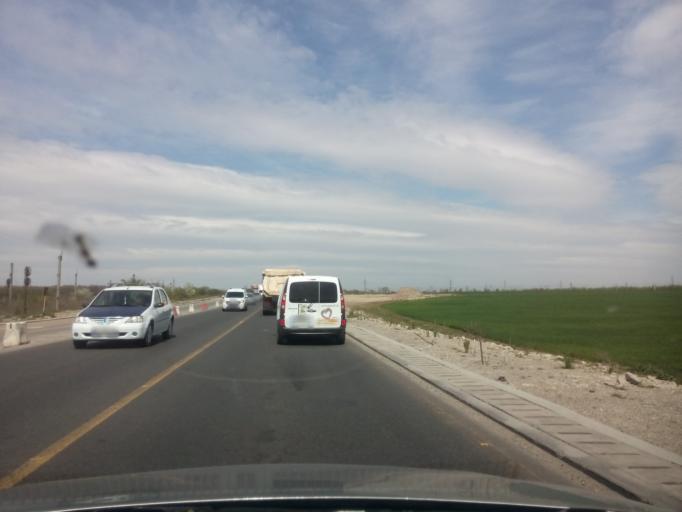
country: RO
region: Ilfov
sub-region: Comuna Pantelimon
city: Pantelimon
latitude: 44.4683
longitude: 26.2326
